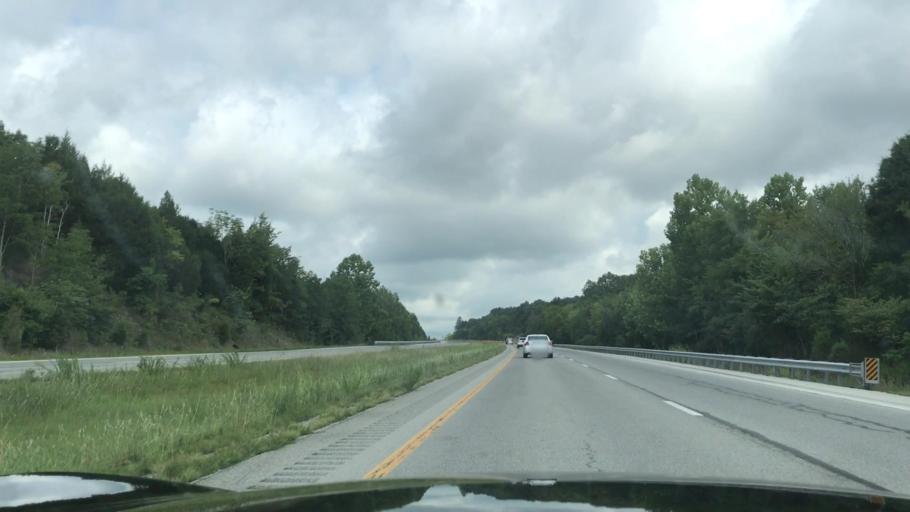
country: US
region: Kentucky
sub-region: Butler County
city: Morgantown
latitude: 37.0905
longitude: -86.6267
